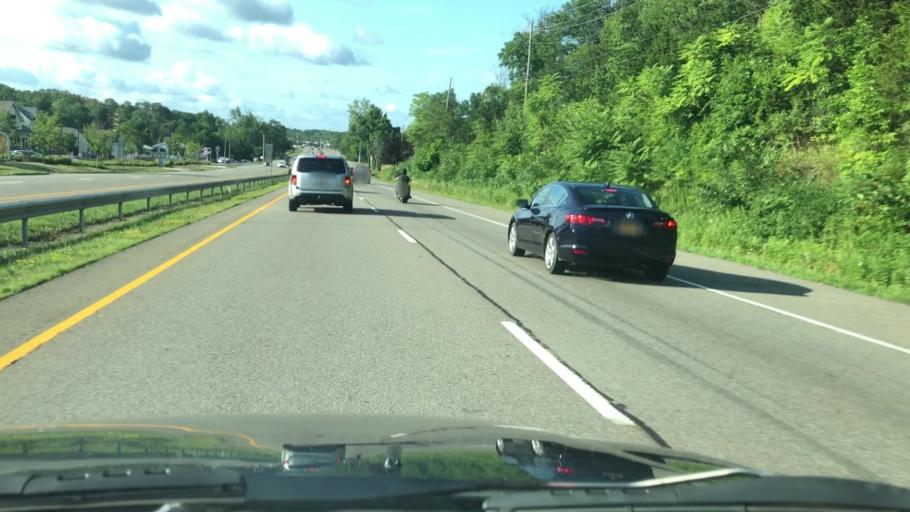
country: US
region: New York
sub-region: Dutchess County
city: Wappingers Falls
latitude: 41.5810
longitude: -73.9087
